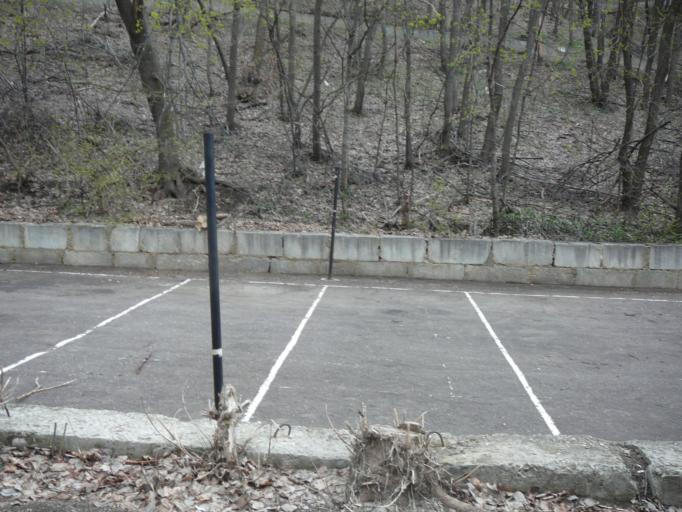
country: RU
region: Saratov
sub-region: Saratovskiy Rayon
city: Saratov
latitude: 51.5485
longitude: 45.9544
